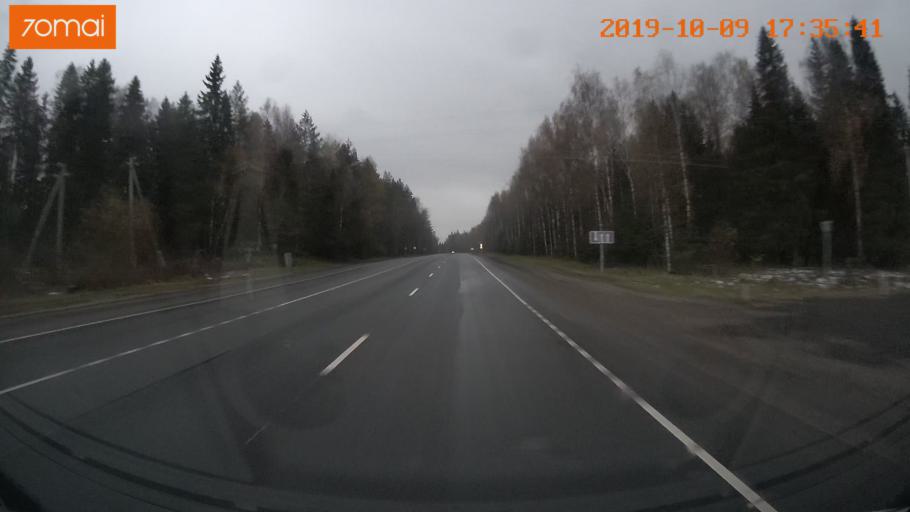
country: RU
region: Ivanovo
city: Bogorodskoye
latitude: 57.0896
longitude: 41.0004
